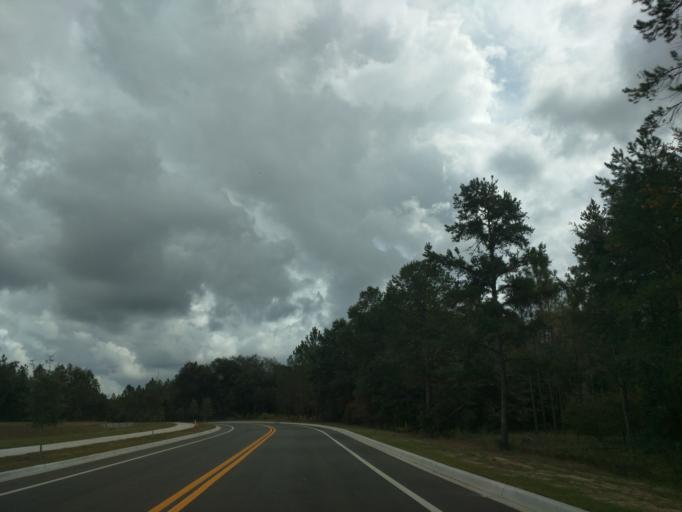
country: US
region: Florida
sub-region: Leon County
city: Woodville
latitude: 30.3818
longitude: -84.2153
